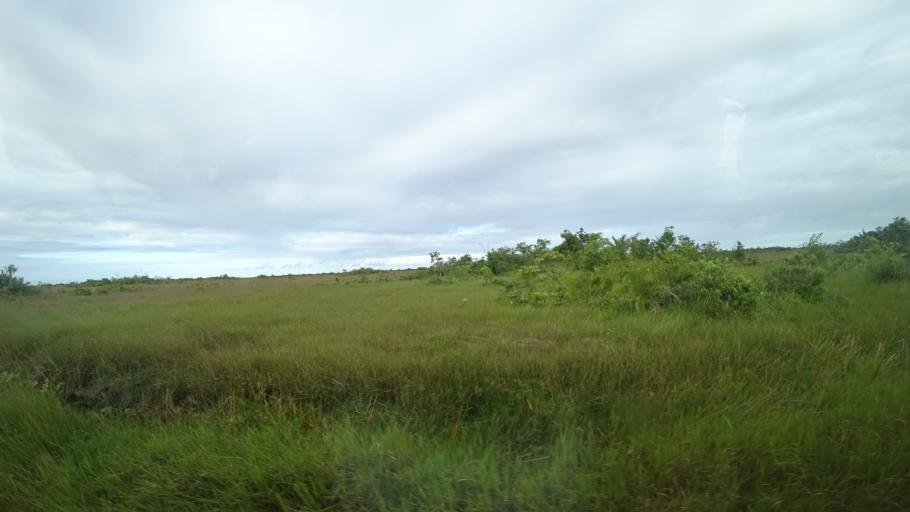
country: MZ
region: Sofala
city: Beira
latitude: -19.7017
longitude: 35.0251
